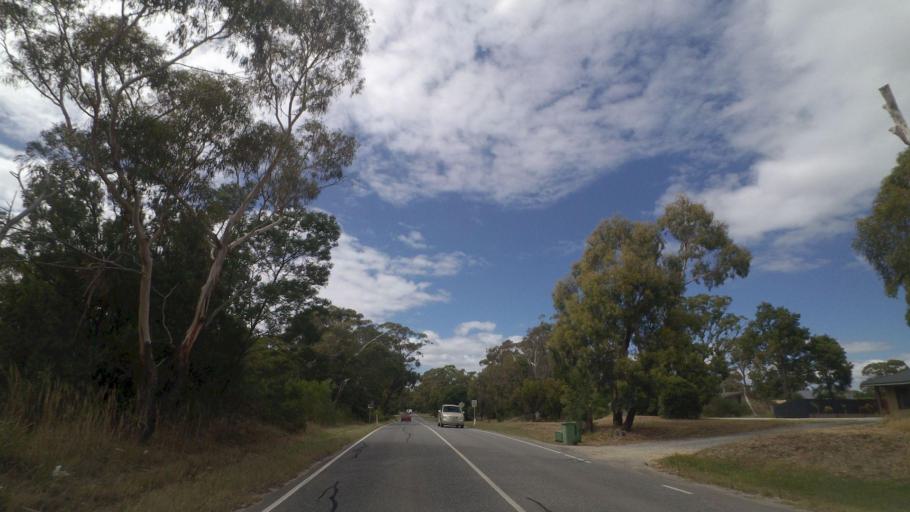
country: AU
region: Victoria
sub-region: Cardinia
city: Koo-Wee-Rup
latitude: -38.2714
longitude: 145.5688
